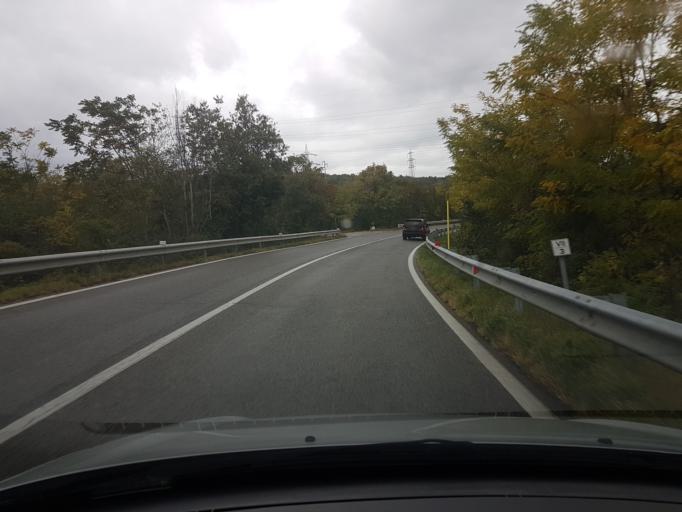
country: IT
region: Friuli Venezia Giulia
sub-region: Provincia di Gorizia
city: Monfalcone
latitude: 45.8145
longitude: 13.5737
